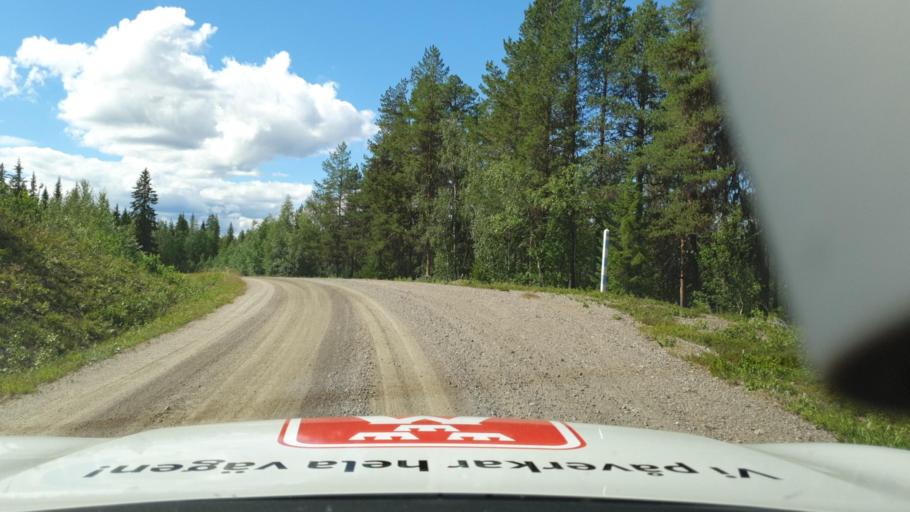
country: SE
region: Vaesterbotten
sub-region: Sorsele Kommun
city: Sorsele
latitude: 65.6712
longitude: 17.2213
